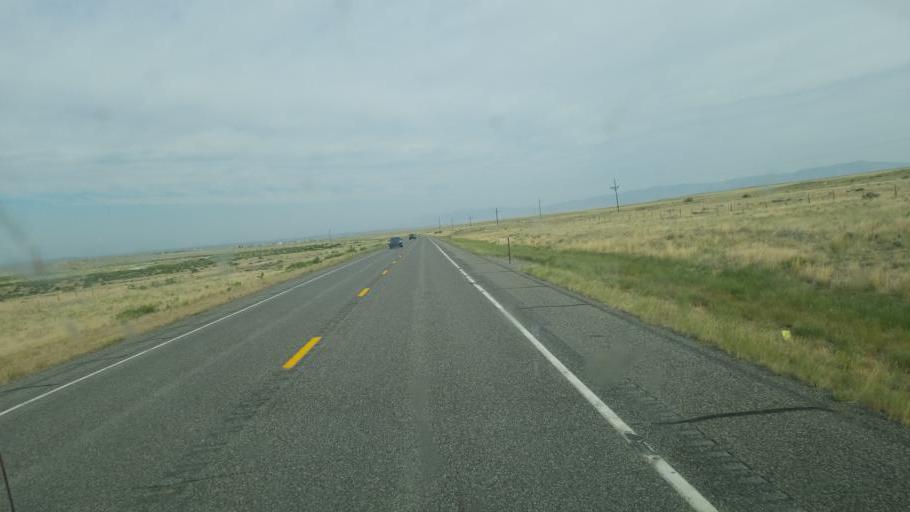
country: US
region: Wyoming
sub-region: Fremont County
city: Riverton
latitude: 43.2300
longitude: -108.0597
